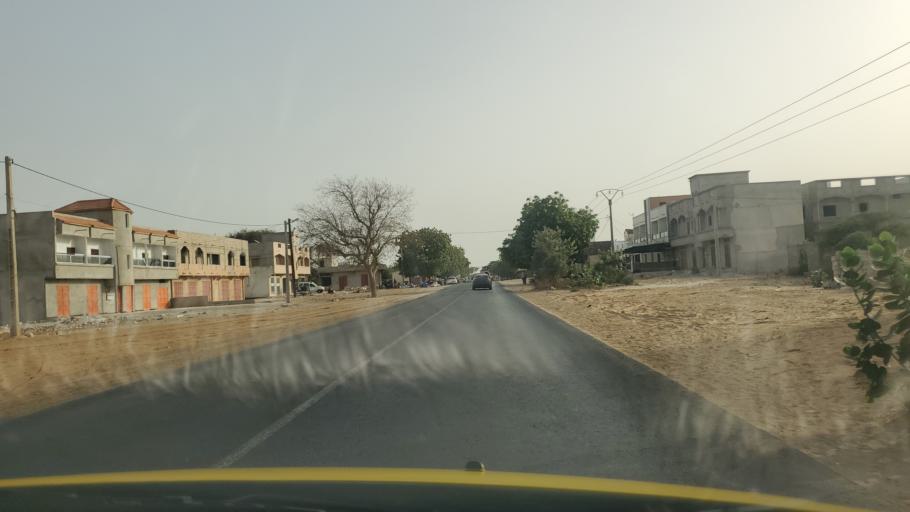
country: SN
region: Thies
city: Mekhe
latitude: 15.1039
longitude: -16.6445
